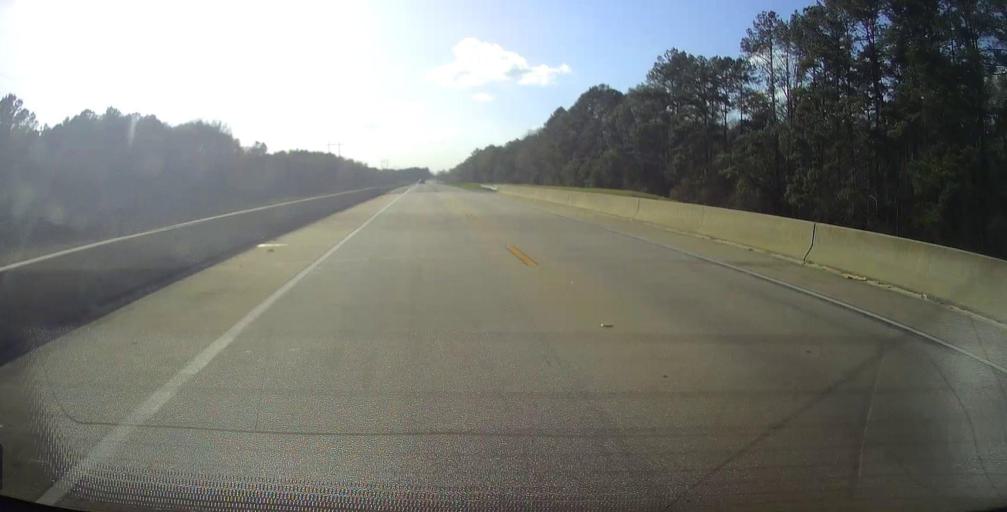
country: US
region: Georgia
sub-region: Montgomery County
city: Mount Vernon
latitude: 32.1915
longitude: -82.6207
